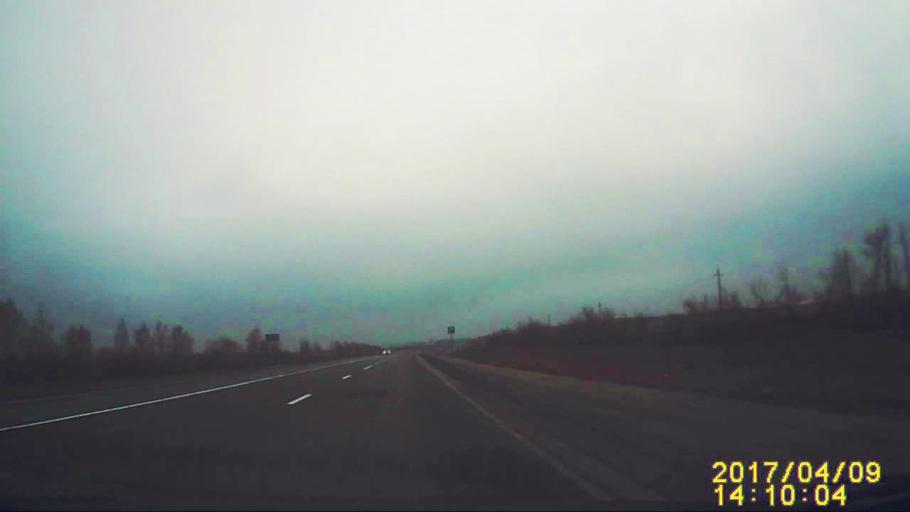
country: RU
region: Ulyanovsk
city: Krasnyy Gulyay
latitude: 54.0345
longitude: 48.2129
